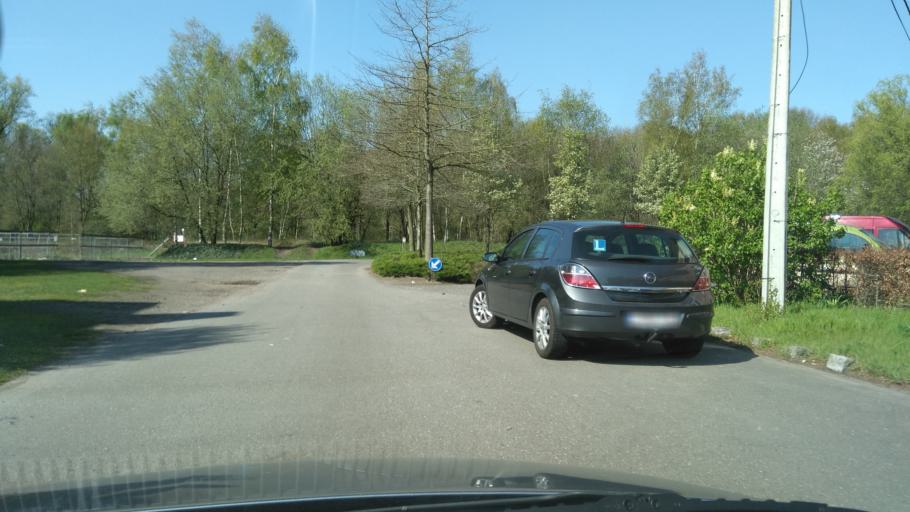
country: BE
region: Flanders
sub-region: Provincie Antwerpen
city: Baarle-Hertog
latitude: 51.3989
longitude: 4.9351
